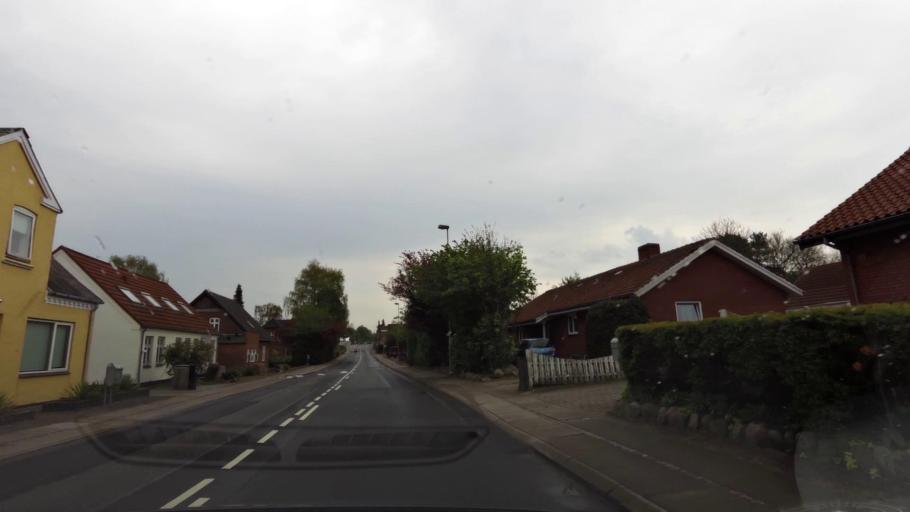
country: DK
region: South Denmark
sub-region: Svendborg Kommune
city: Thuro By
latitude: 55.1548
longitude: 10.6698
